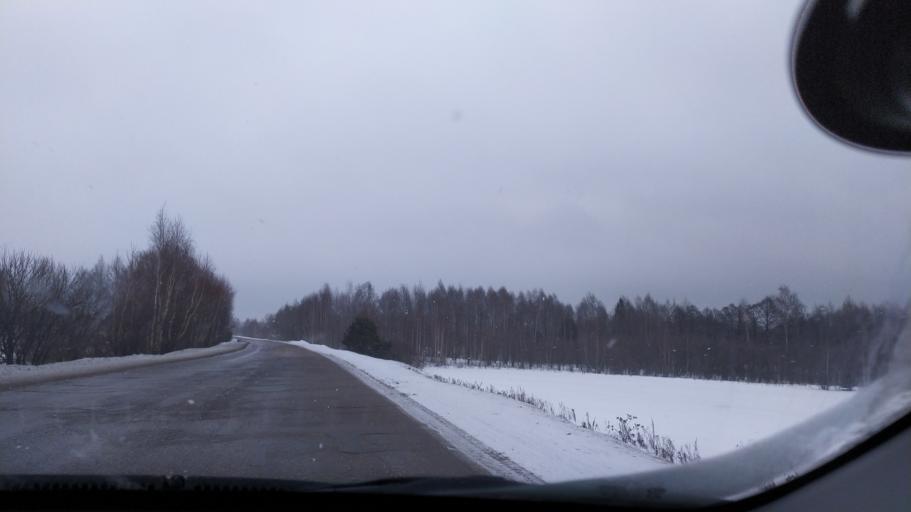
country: RU
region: Mariy-El
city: Krasnogorskiy
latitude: 56.1536
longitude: 48.1580
